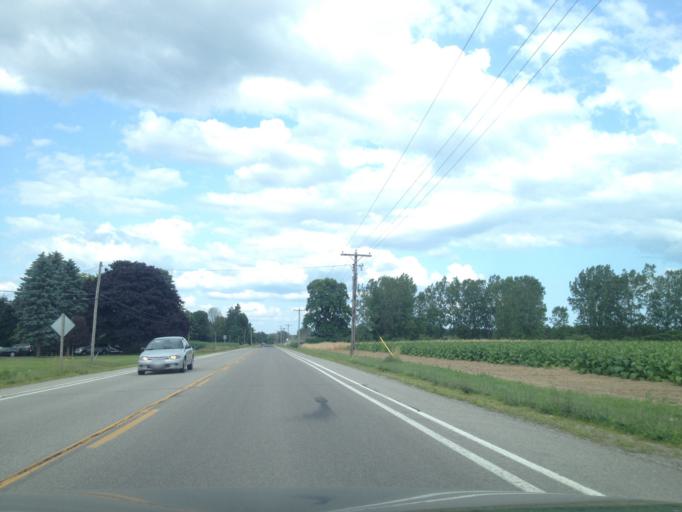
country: CA
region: Ontario
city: Aylmer
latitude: 42.6626
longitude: -81.0036
